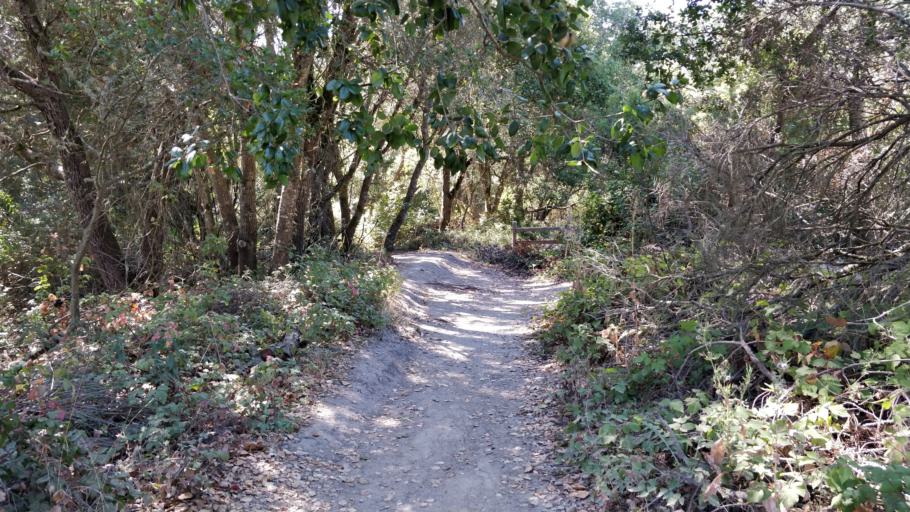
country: US
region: California
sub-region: Contra Costa County
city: Kensington
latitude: 37.9052
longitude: -122.2601
